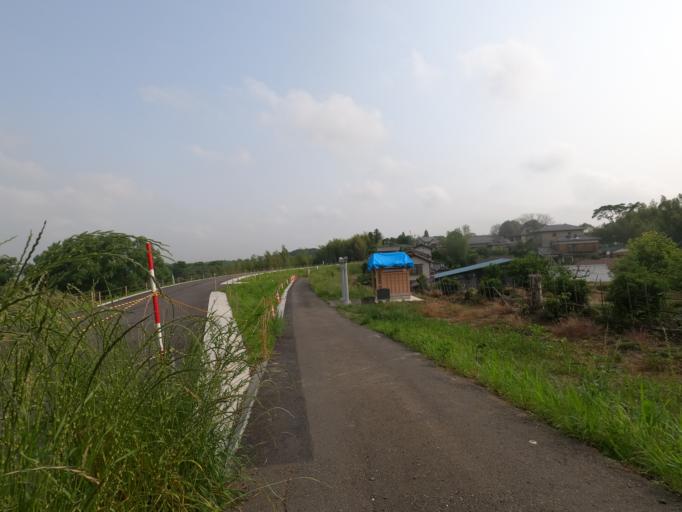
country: JP
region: Ibaraki
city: Moriya
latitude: 35.9608
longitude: 139.9504
